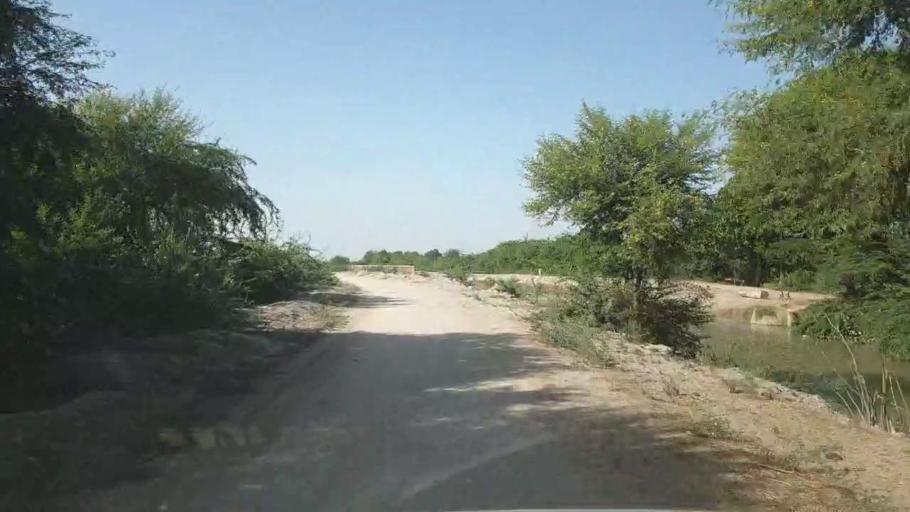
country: PK
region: Sindh
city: Kadhan
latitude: 24.5722
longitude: 68.9874
